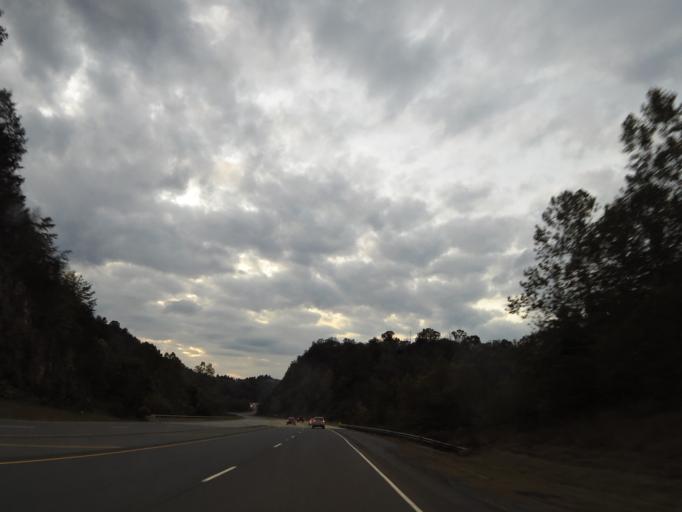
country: US
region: North Carolina
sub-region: Madison County
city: Marshall
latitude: 35.7683
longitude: -82.6172
